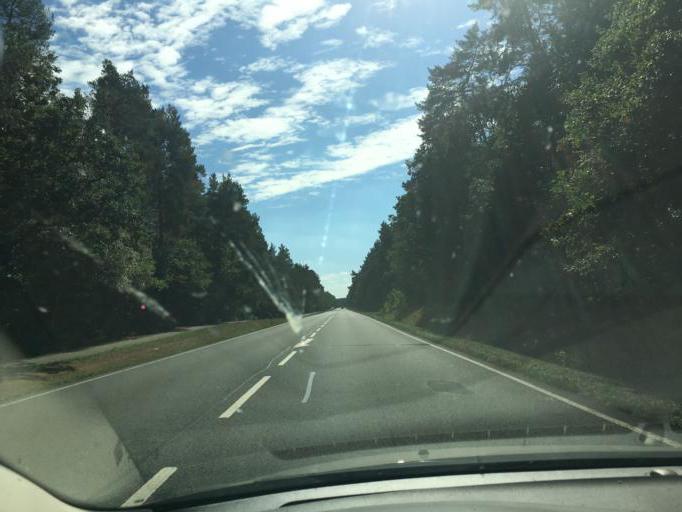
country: DE
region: Saxony-Anhalt
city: Seehausen
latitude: 52.8436
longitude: 11.7321
